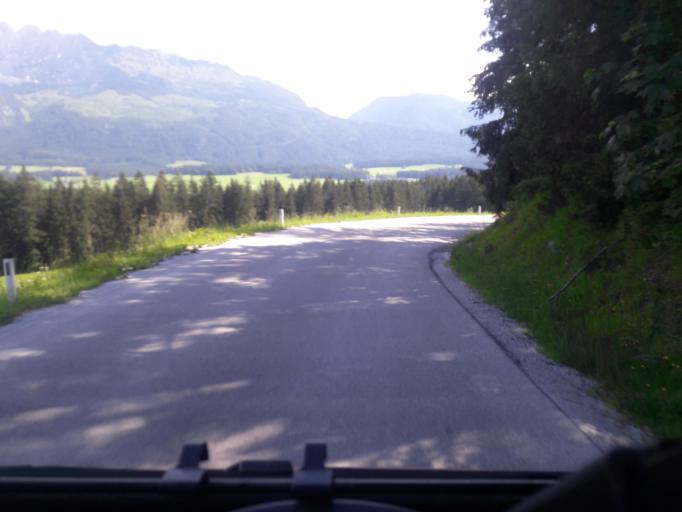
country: AT
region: Styria
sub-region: Politischer Bezirk Liezen
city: Tauplitz
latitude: 47.5673
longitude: 13.9570
